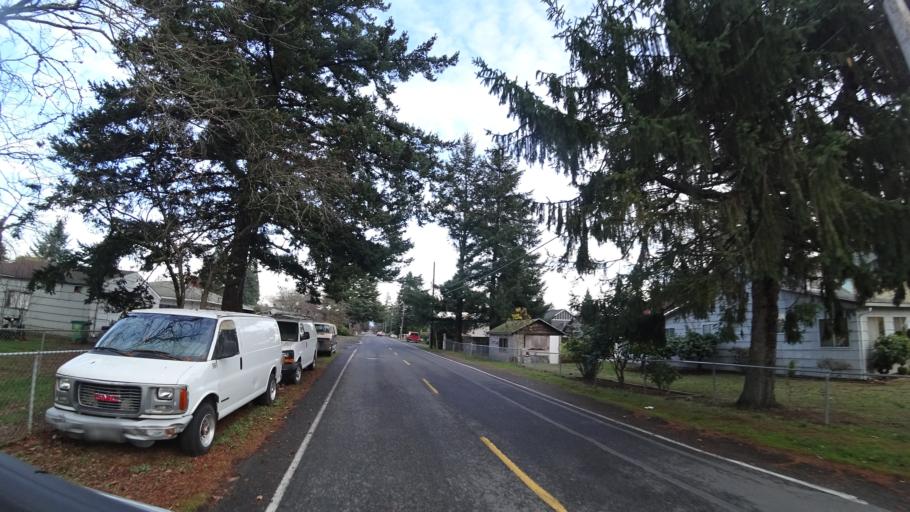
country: US
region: Oregon
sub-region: Multnomah County
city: Lents
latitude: 45.5139
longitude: -122.5209
